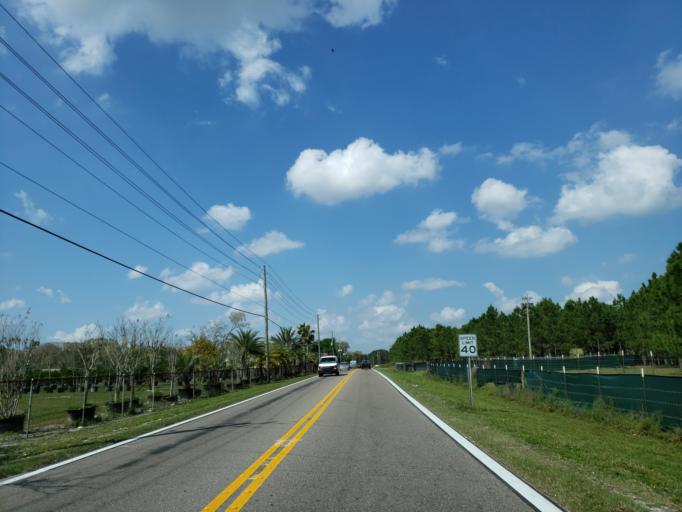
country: US
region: Florida
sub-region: Hillsborough County
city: Keystone
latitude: 28.1436
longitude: -82.5773
